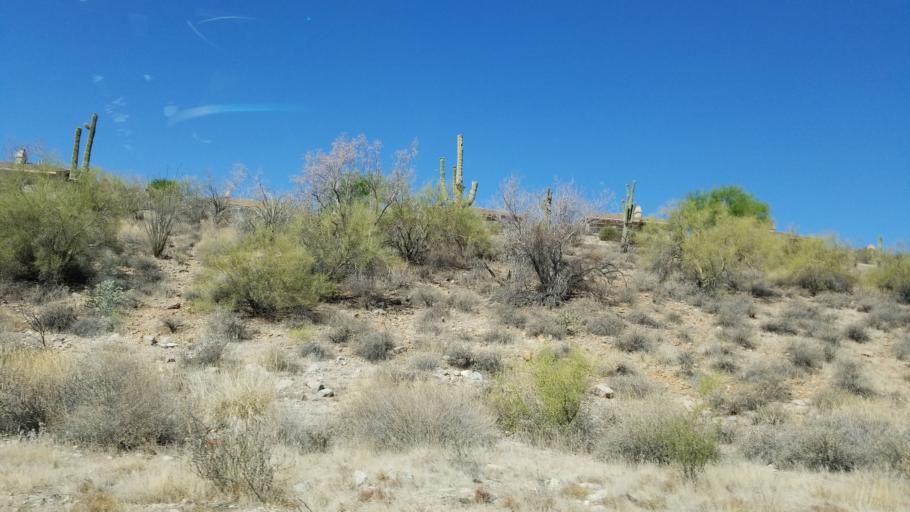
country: US
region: Arizona
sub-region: Maricopa County
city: Fountain Hills
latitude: 33.5990
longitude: -111.7571
